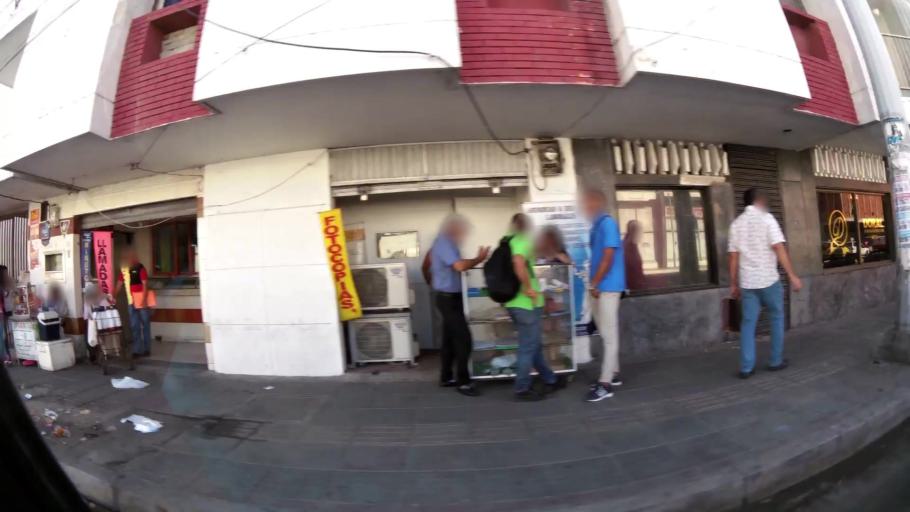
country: CO
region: Atlantico
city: Barranquilla
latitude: 10.9851
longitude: -74.7854
